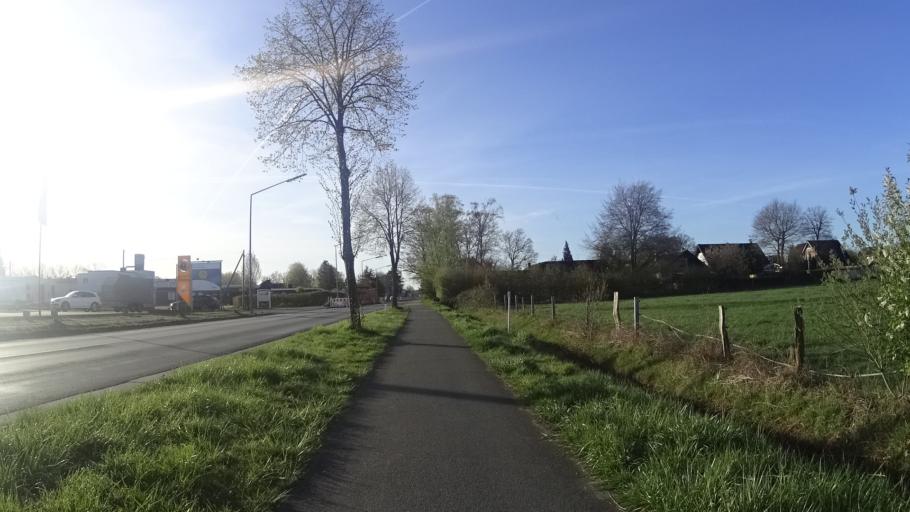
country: DE
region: North Rhine-Westphalia
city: Emsdetten
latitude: 52.1365
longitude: 7.5429
